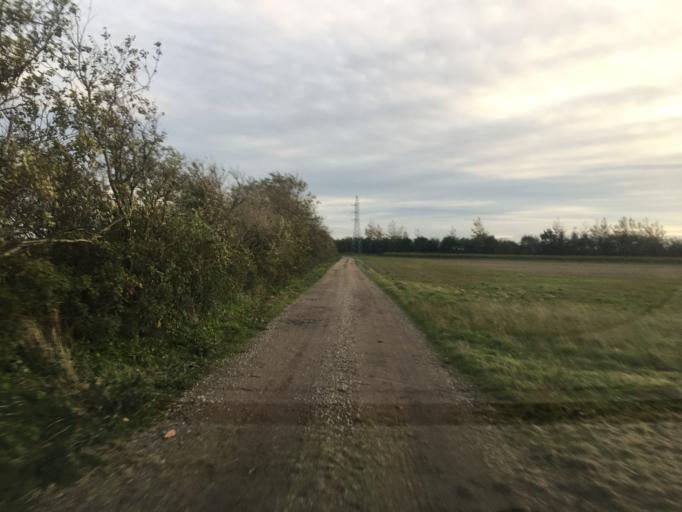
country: DK
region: South Denmark
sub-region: Tonder Kommune
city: Tonder
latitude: 54.9571
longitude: 8.8419
